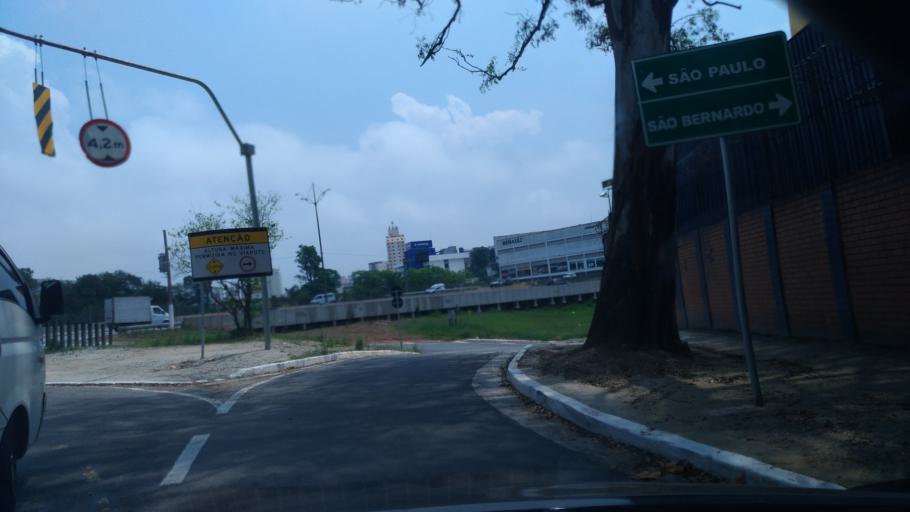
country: BR
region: Sao Paulo
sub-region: Sao Bernardo Do Campo
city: Sao Bernardo do Campo
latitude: -23.7181
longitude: -46.5574
